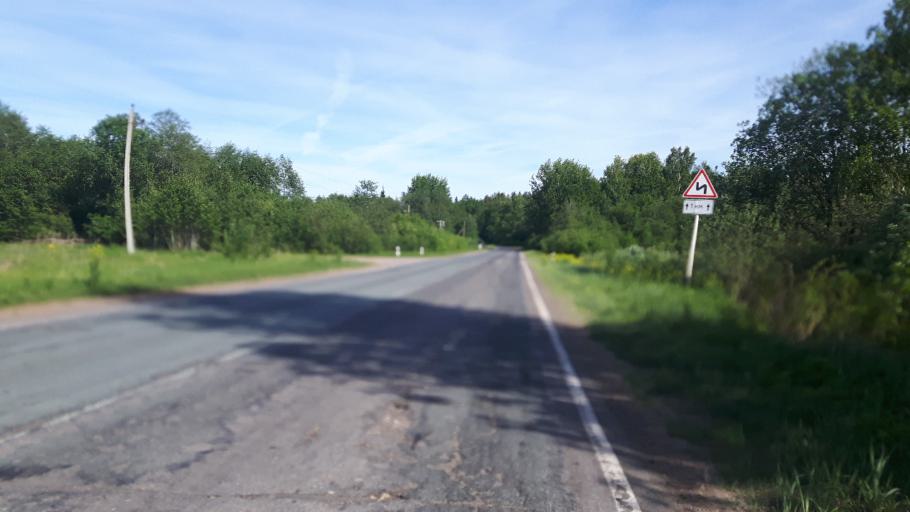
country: RU
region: Leningrad
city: Ivangorod
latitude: 59.4174
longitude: 28.3648
